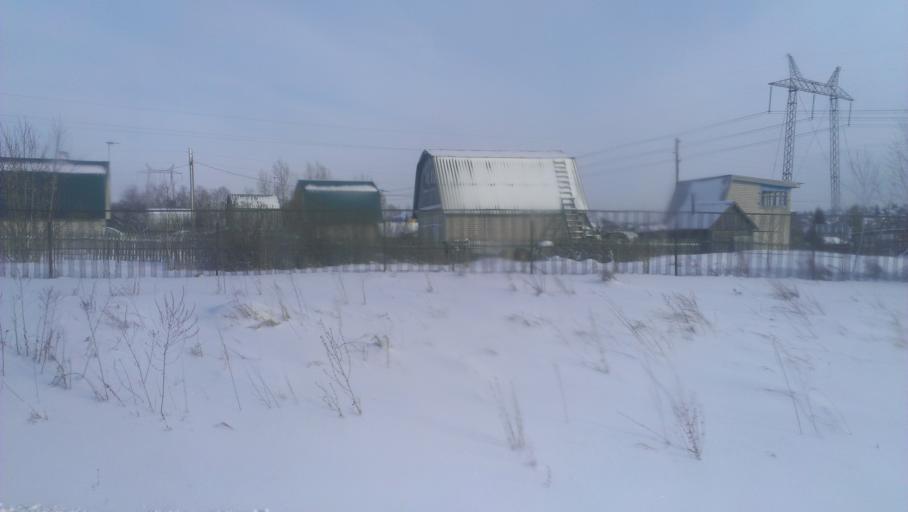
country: RU
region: Altai Krai
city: Gon'ba
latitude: 53.4170
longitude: 83.5496
